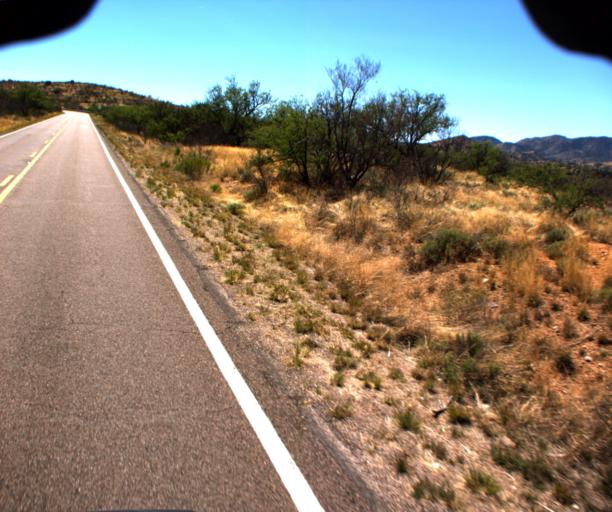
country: US
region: Arizona
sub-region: Pima County
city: Corona de Tucson
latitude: 31.8502
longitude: -110.6979
